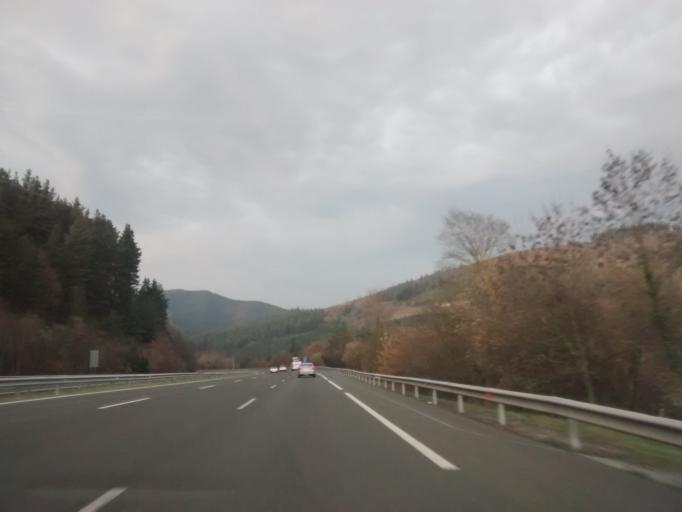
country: ES
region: Basque Country
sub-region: Provincia de Alava
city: Lezama
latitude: 43.0456
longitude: -2.9232
